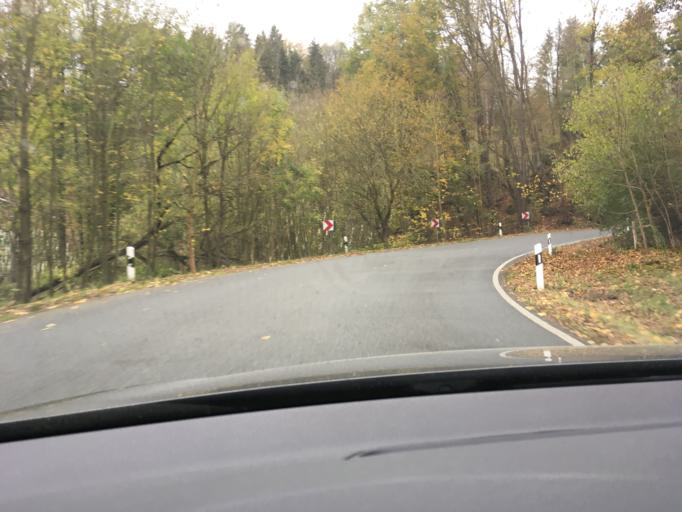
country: DE
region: Saxony
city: Glashutte
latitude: 50.8886
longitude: 13.8034
